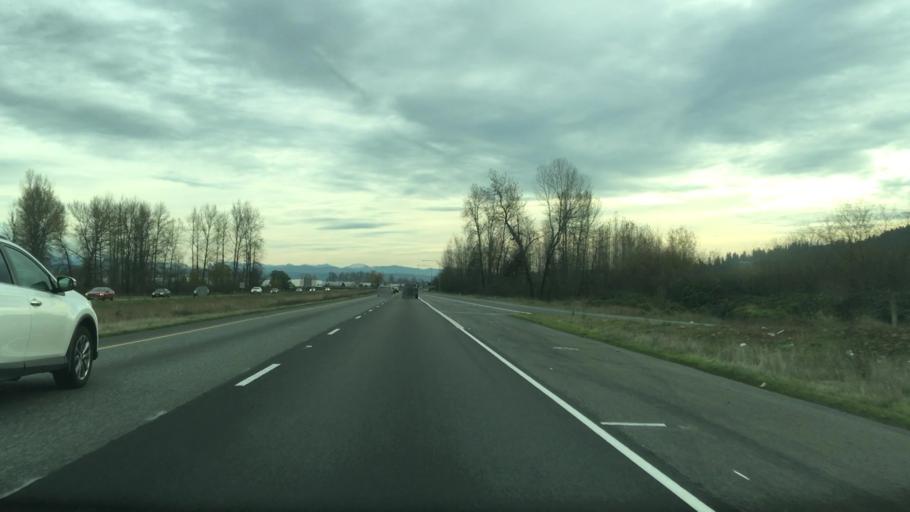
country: US
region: Washington
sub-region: Pierce County
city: Sumner
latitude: 47.2319
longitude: -122.2505
